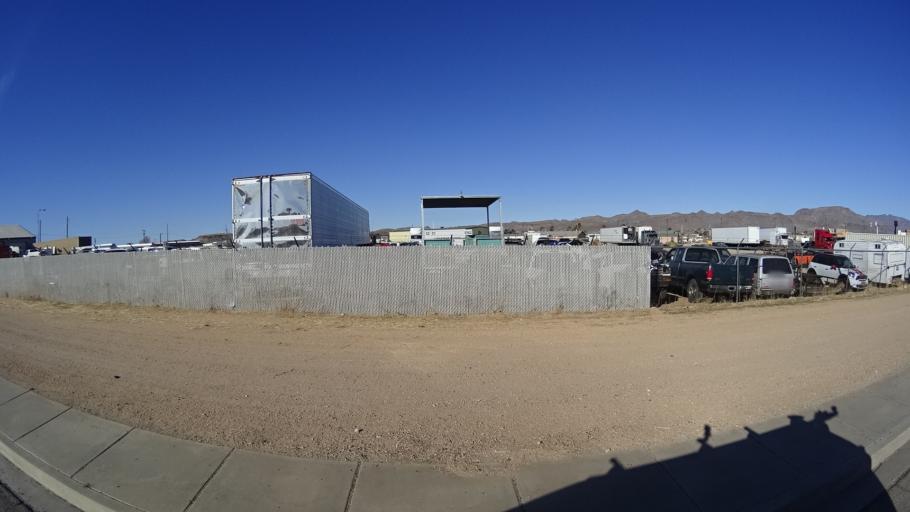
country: US
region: Arizona
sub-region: Mohave County
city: Kingman
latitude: 35.2111
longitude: -114.0114
